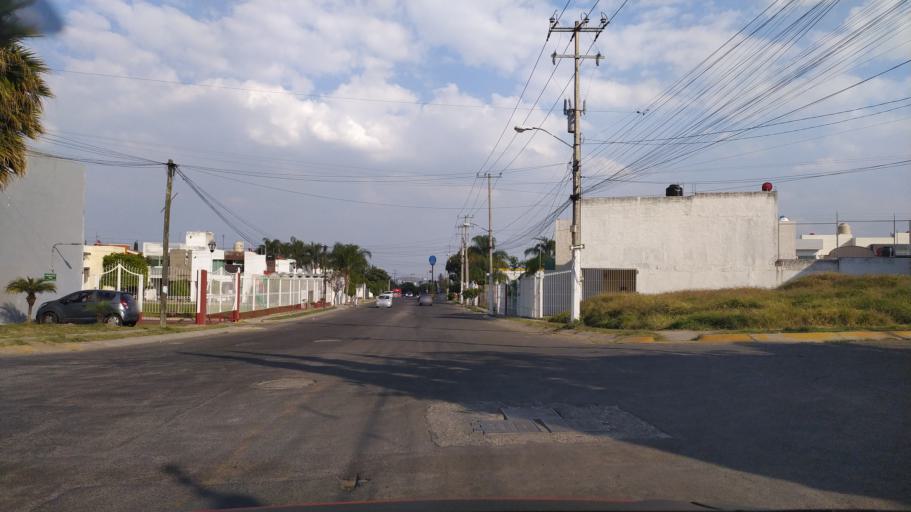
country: MX
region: Jalisco
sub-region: Tlajomulco de Zuniga
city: Palomar
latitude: 20.6278
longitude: -103.4700
